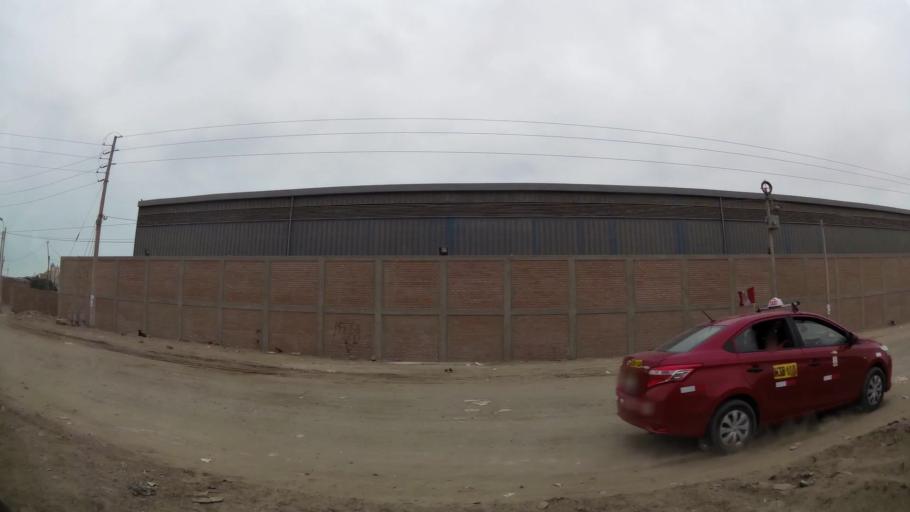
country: PE
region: Lima
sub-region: Lima
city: Surco
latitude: -12.2104
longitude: -76.9681
